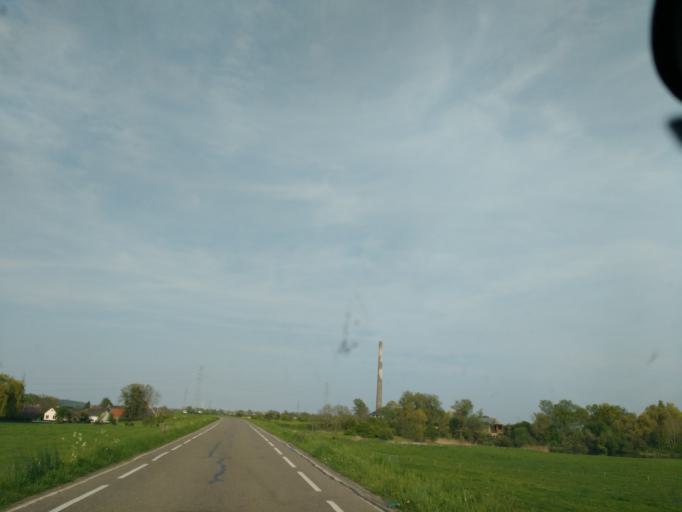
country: NL
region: Gelderland
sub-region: Gemeente Wageningen
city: Wageningen
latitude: 51.9479
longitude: 5.6266
